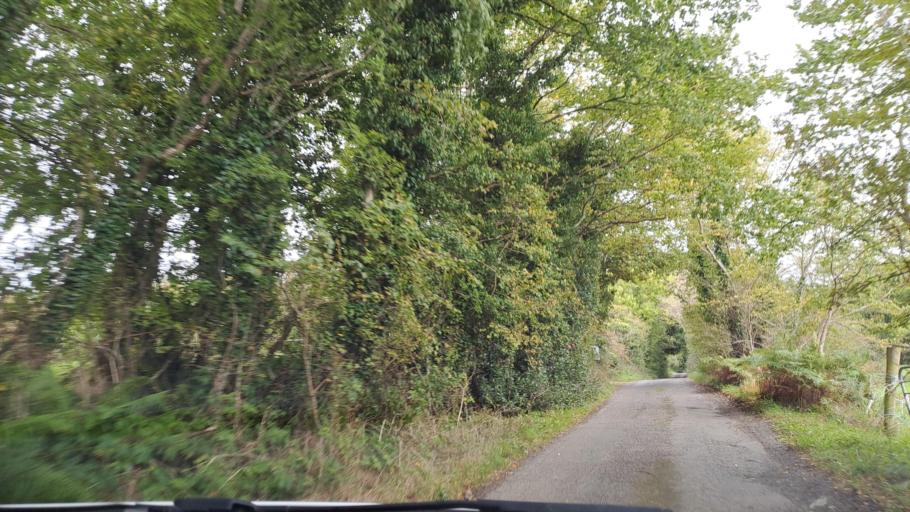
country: IE
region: Ulster
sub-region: An Cabhan
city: Bailieborough
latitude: 54.0058
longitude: -6.9526
